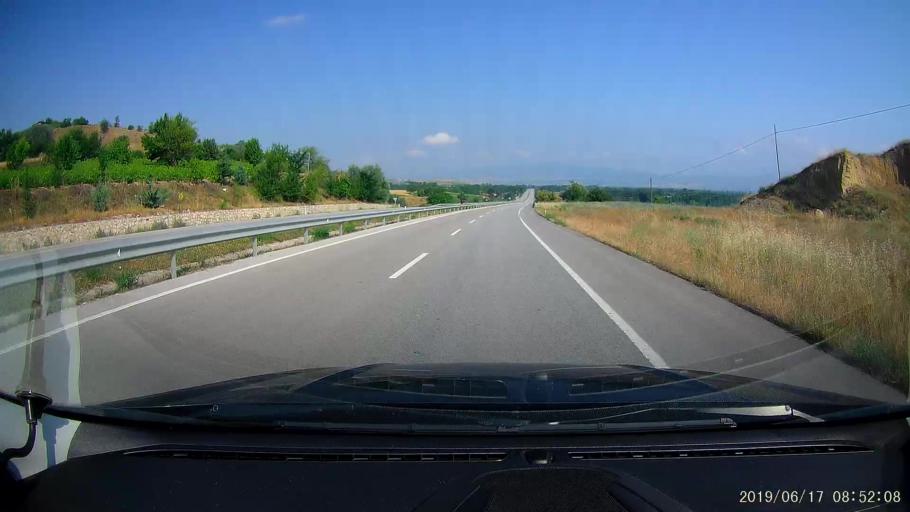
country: TR
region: Tokat
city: Erbaa
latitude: 40.6936
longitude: 36.5017
